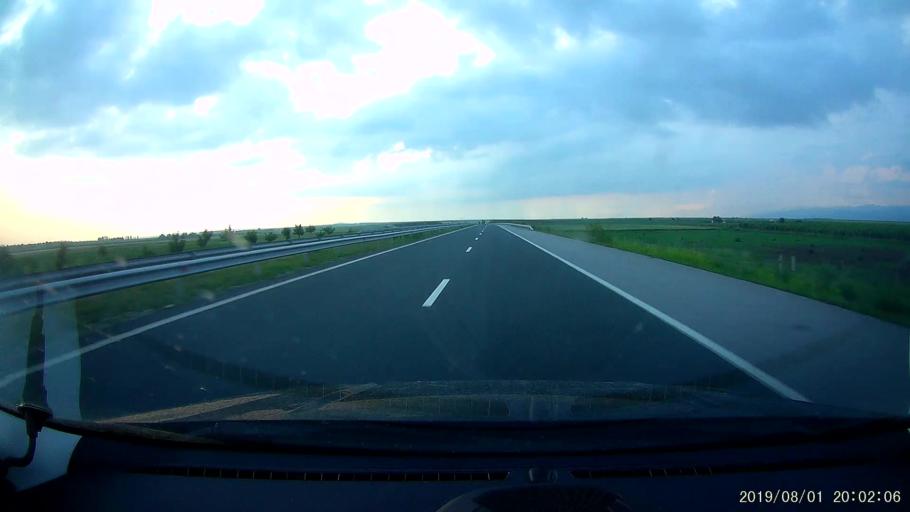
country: BG
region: Yambol
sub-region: Obshtina Straldzha
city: Straldzha
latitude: 42.5584
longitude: 26.6417
